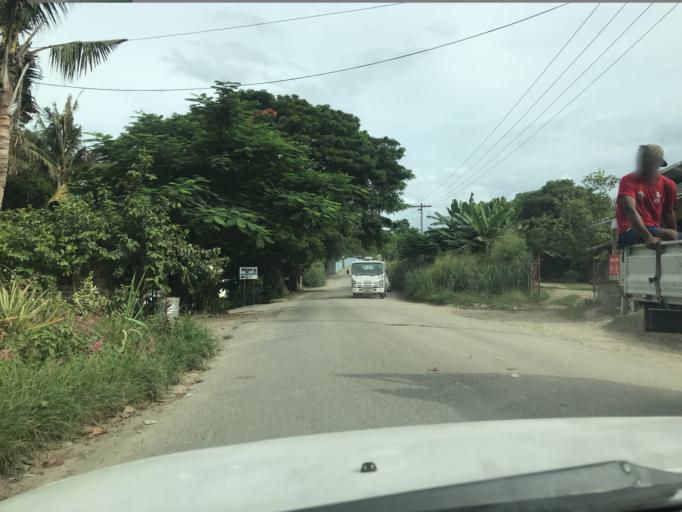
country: SB
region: Guadalcanal
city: Honiara
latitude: -9.4331
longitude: 159.9447
